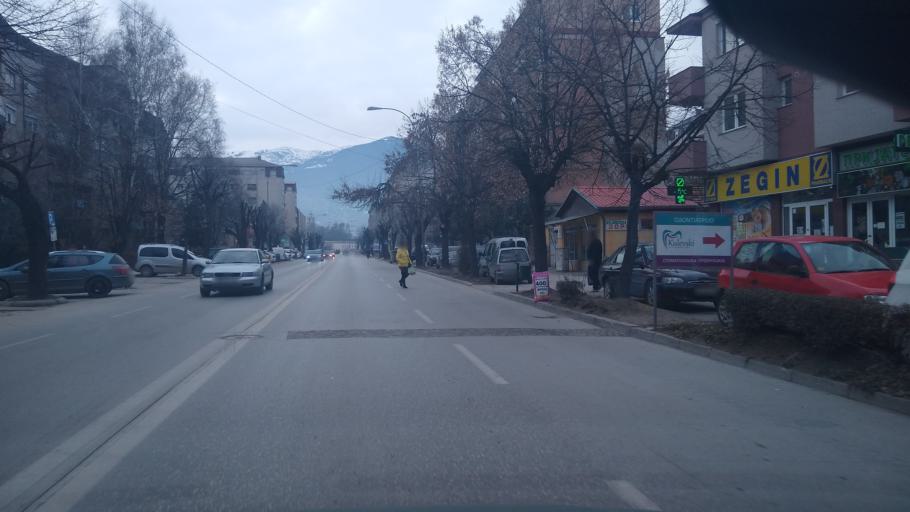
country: MK
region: Bitola
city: Bitola
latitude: 41.0346
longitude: 21.3393
